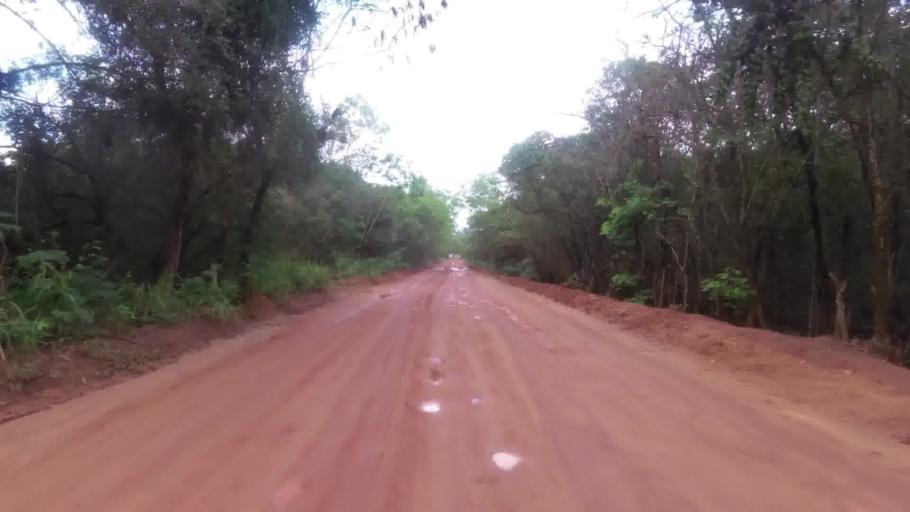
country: BR
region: Espirito Santo
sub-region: Piuma
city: Piuma
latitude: -20.7900
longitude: -40.6331
